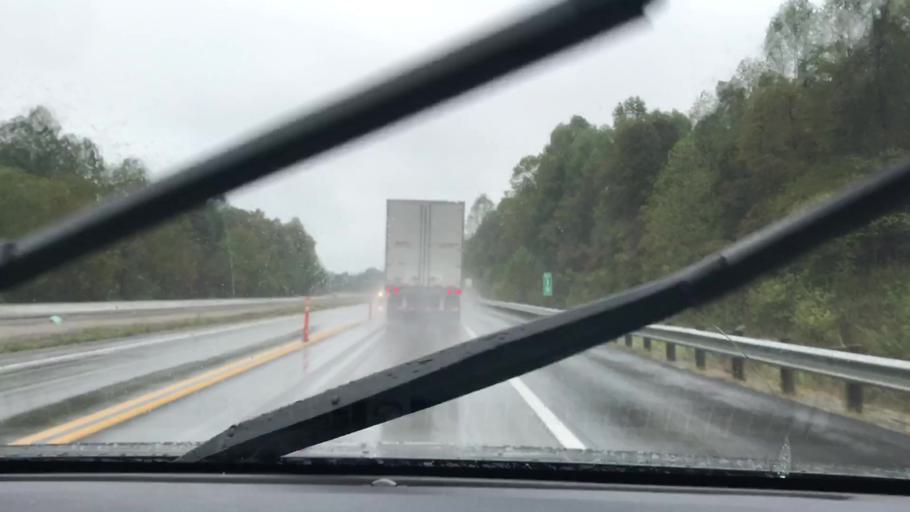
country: US
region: Kentucky
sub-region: Christian County
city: Hopkinsville
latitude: 36.9993
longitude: -87.4646
